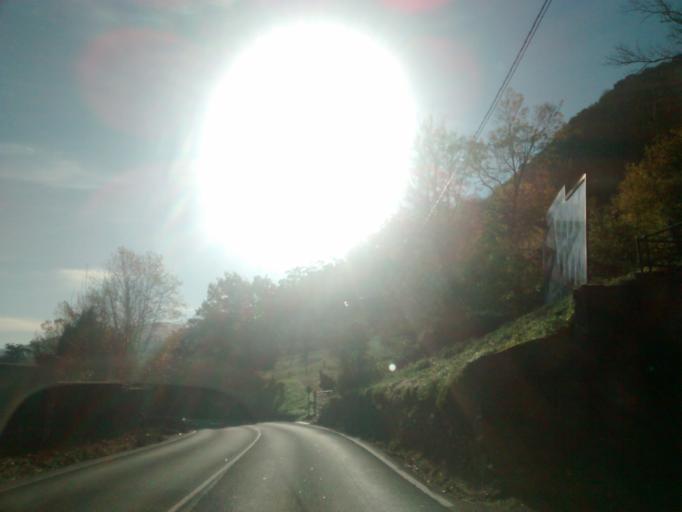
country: ES
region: Cantabria
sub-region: Provincia de Cantabria
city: Puente Viesgo
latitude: 43.2959
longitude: -3.9660
